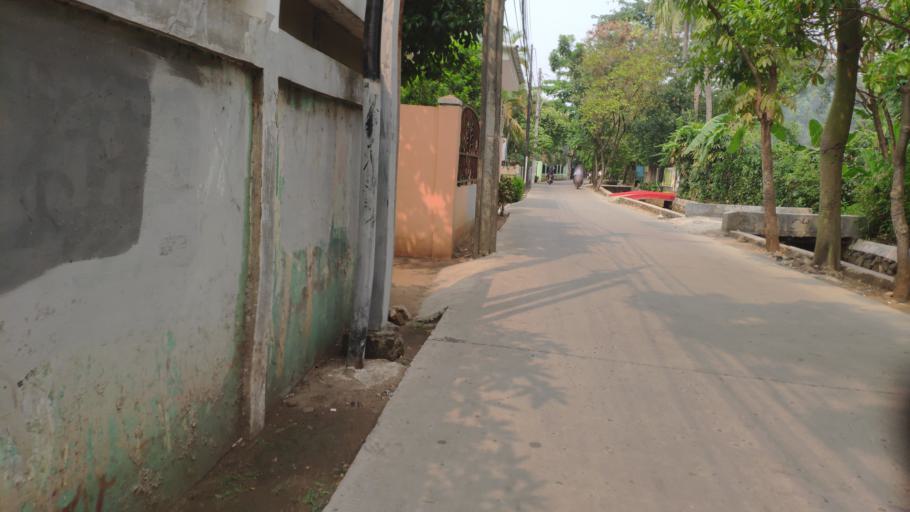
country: ID
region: West Java
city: Depok
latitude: -6.3504
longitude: 106.8082
